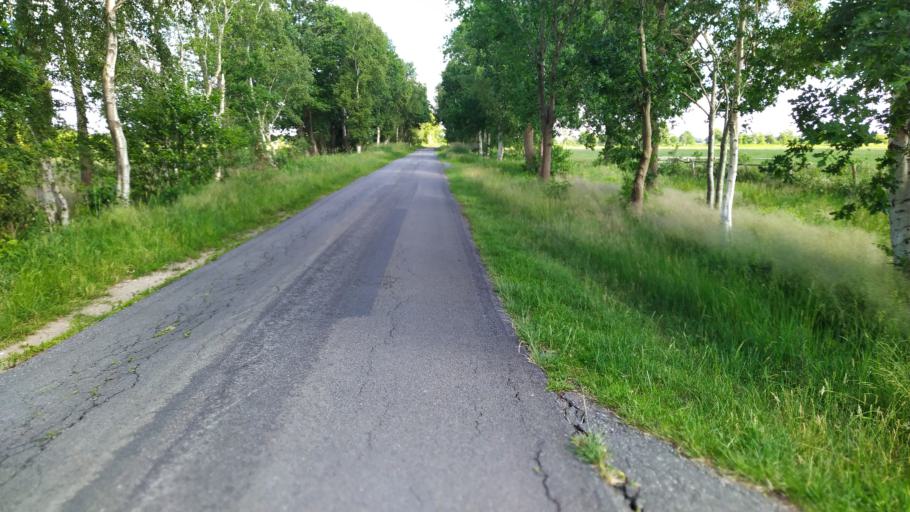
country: DE
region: Lower Saxony
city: Steinau
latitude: 53.6490
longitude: 8.9050
